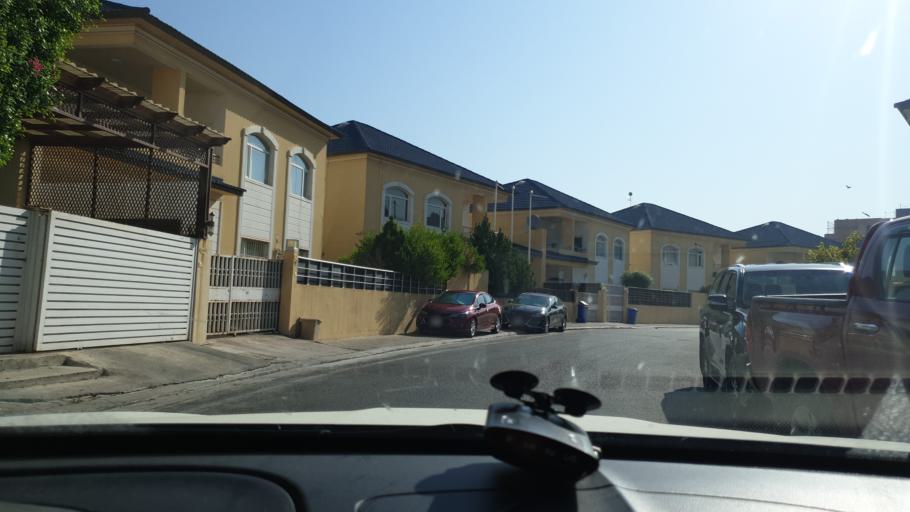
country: IQ
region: Arbil
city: Erbil
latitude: 36.1894
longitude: 43.9706
